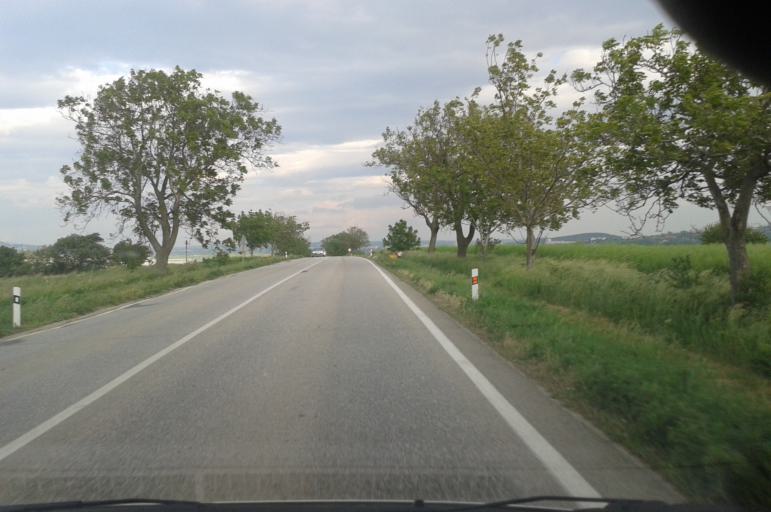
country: SK
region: Nitriansky
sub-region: Okres Nitra
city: Nitra
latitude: 48.3309
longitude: 18.0131
